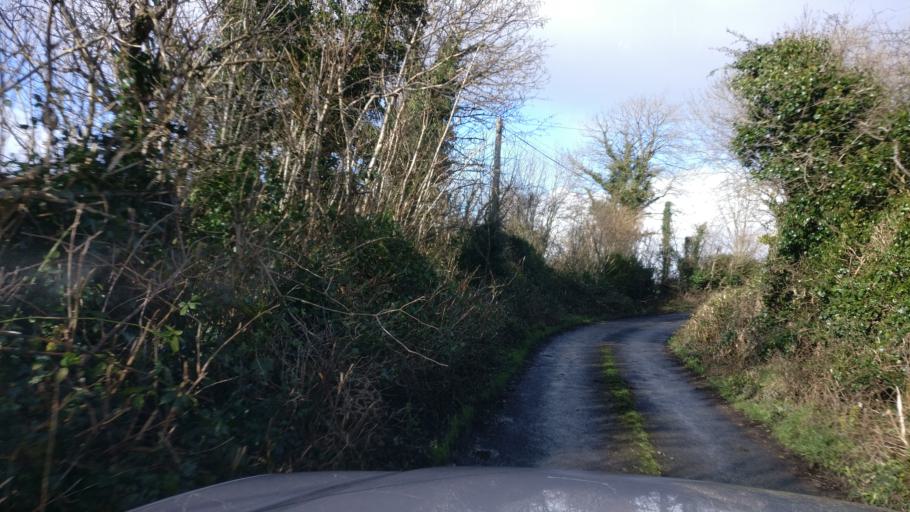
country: IE
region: Connaught
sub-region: County Galway
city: Athenry
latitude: 53.2290
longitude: -8.7577
